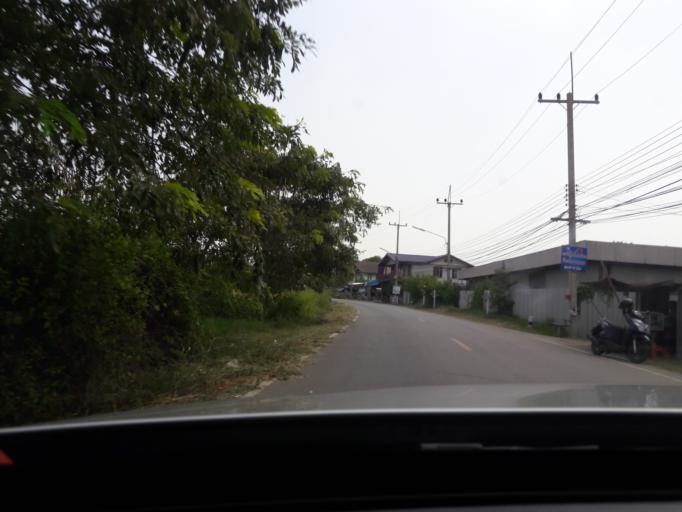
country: TH
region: Samut Songkhram
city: Amphawa
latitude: 13.3376
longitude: 99.9603
